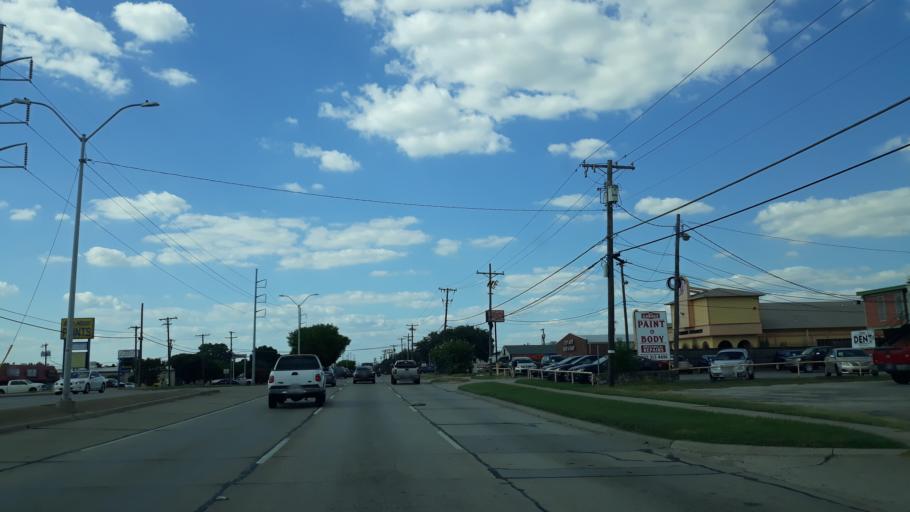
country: US
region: Texas
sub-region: Dallas County
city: Irving
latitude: 32.8224
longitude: -96.9937
